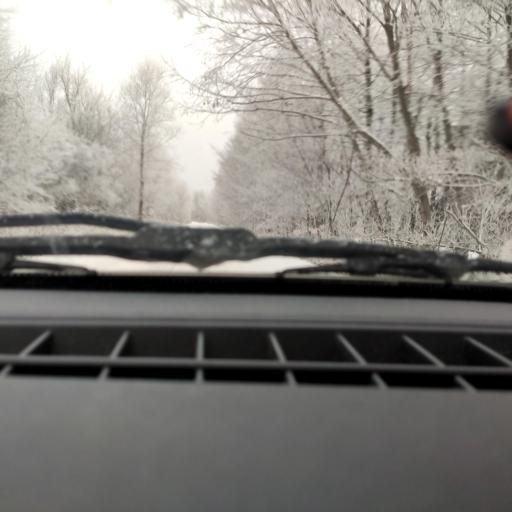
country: RU
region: Bashkortostan
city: Ufa
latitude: 54.7133
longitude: 56.1290
